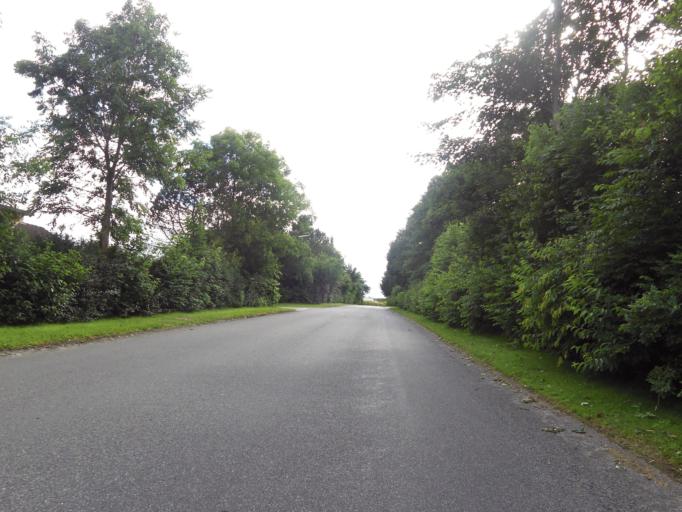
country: DK
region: South Denmark
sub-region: Tonder Kommune
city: Toftlund
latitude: 55.1337
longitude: 9.1241
